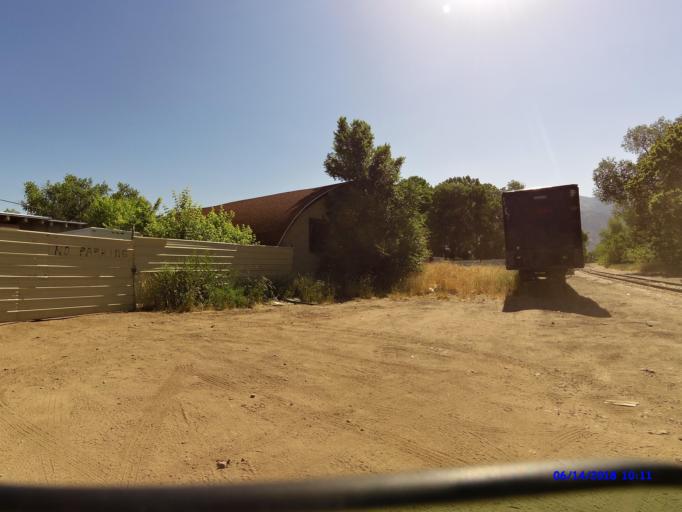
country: US
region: Utah
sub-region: Weber County
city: Ogden
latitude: 41.2247
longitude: -111.9946
